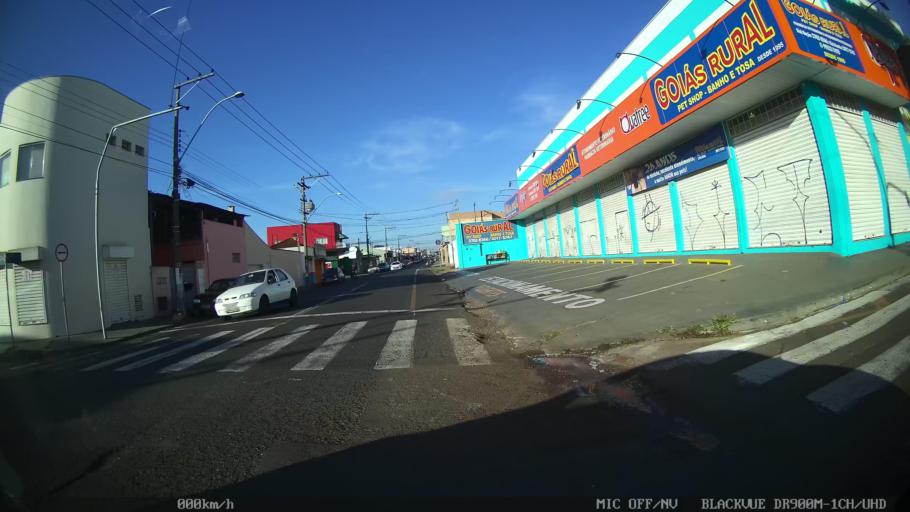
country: BR
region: Sao Paulo
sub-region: Franca
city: Franca
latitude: -20.5425
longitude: -47.3871
